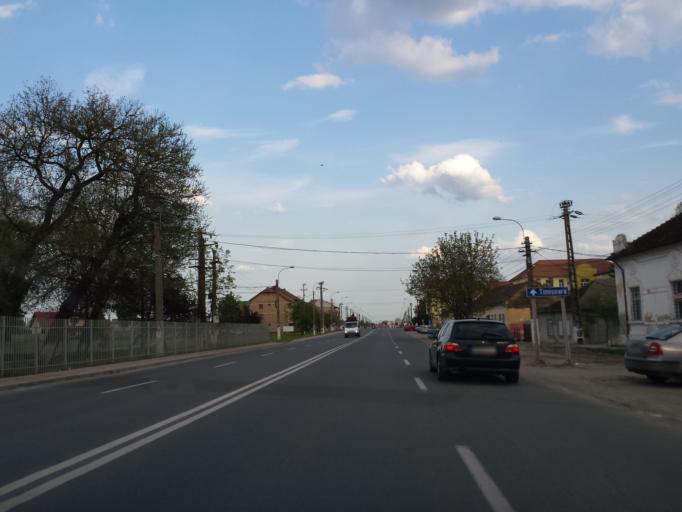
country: RO
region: Timis
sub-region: Oras Sannicolau Mare
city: Sannicolau Mare
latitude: 46.0691
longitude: 20.6341
